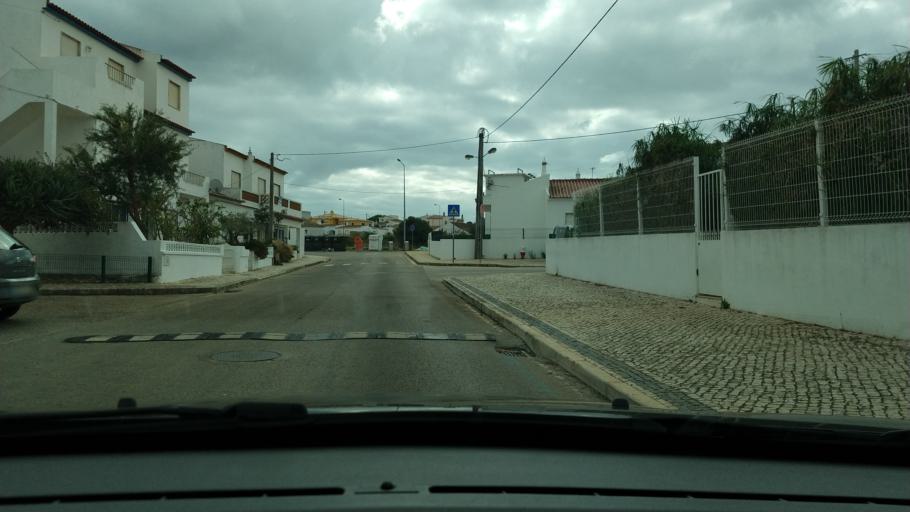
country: PT
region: Faro
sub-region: Lagos
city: Lagos
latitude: 37.0748
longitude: -8.7757
